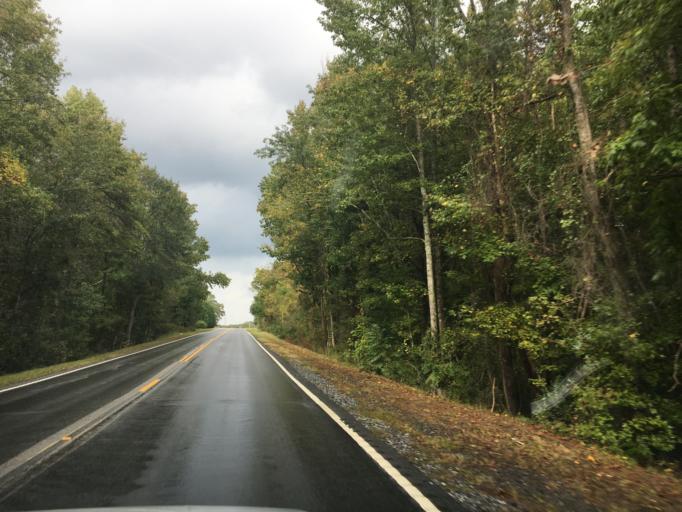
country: US
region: Georgia
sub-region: Hart County
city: Reed Creek
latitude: 34.3945
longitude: -82.8073
